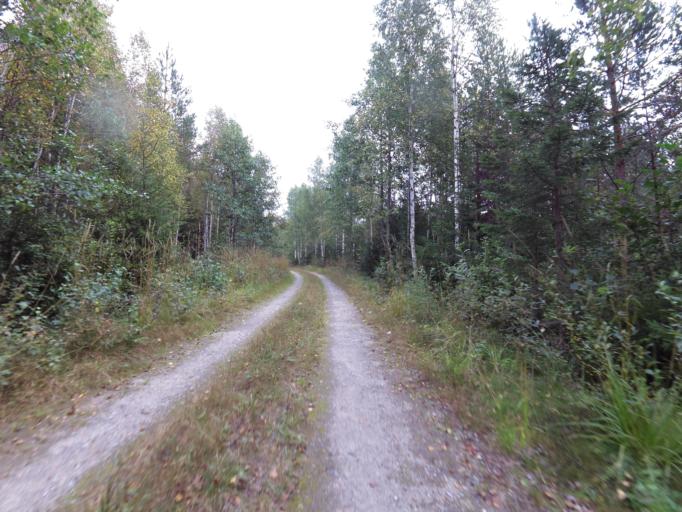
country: SE
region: Gaevleborg
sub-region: Gavle Kommun
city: Valbo
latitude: 60.7209
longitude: 17.0399
